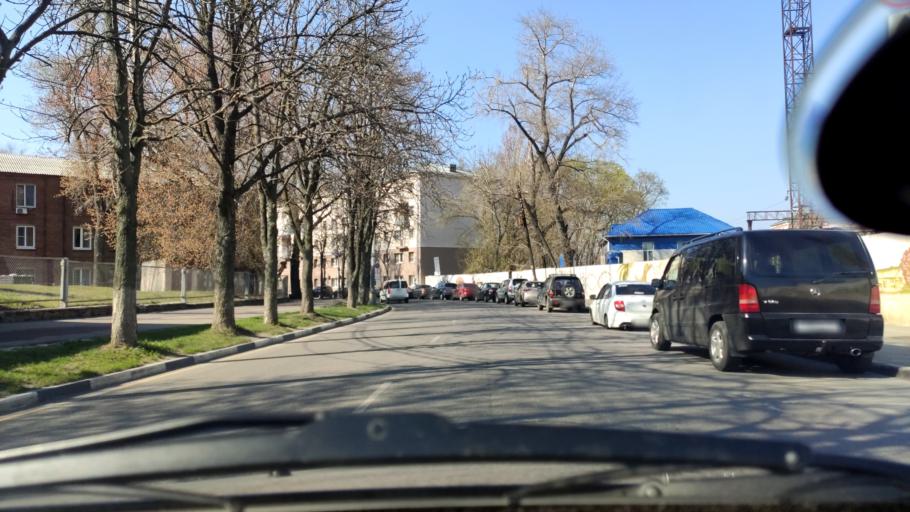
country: RU
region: Voronezj
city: Voronezh
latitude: 51.6815
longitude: 39.2140
